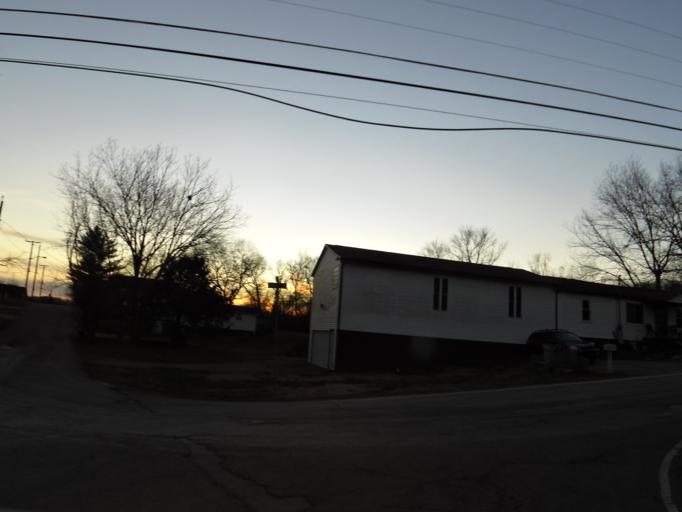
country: US
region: Tennessee
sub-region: Knox County
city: Knoxville
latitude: 35.9839
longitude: -83.9613
